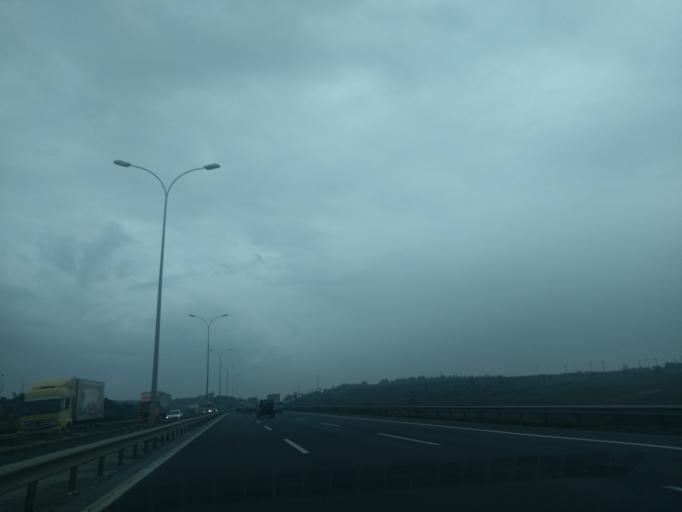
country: TR
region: Istanbul
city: Bueyuekcekmece
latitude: 41.1014
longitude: 28.6058
